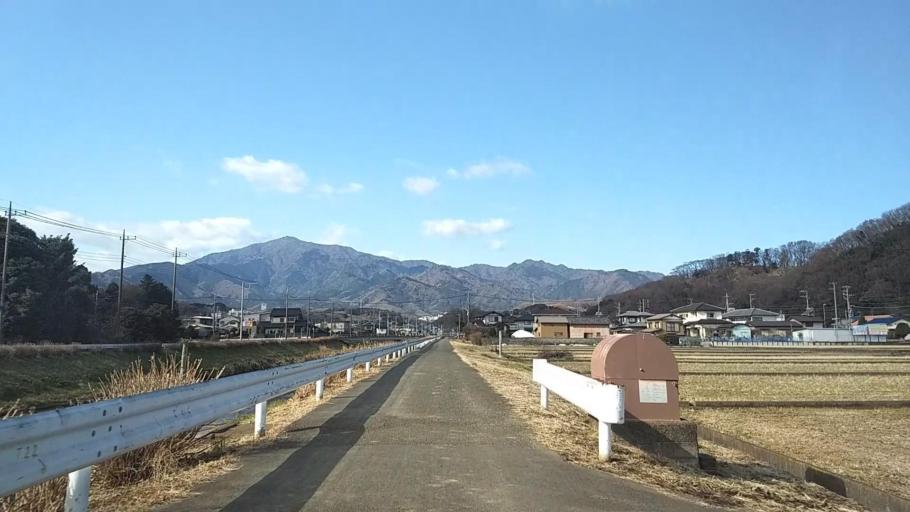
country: JP
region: Kanagawa
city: Atsugi
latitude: 35.4327
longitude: 139.3218
